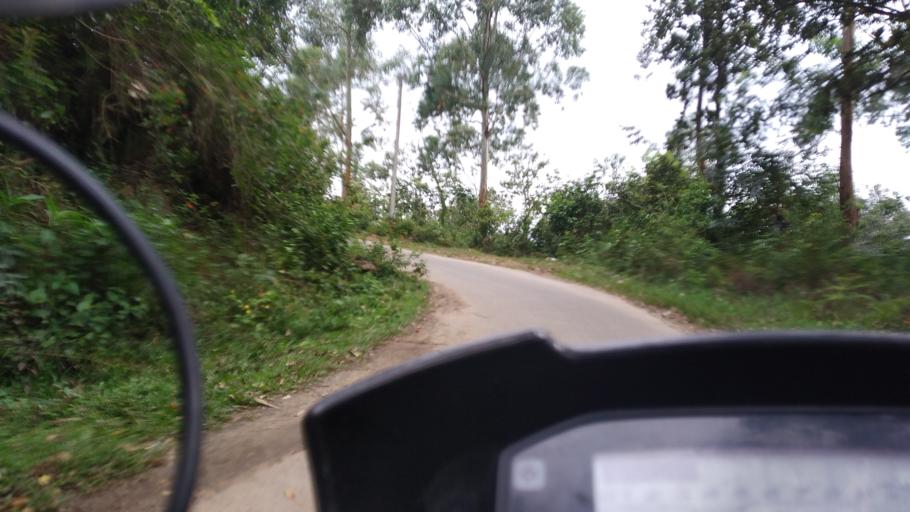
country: IN
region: Kerala
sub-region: Idukki
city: Munnar
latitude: 10.0392
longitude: 77.1735
